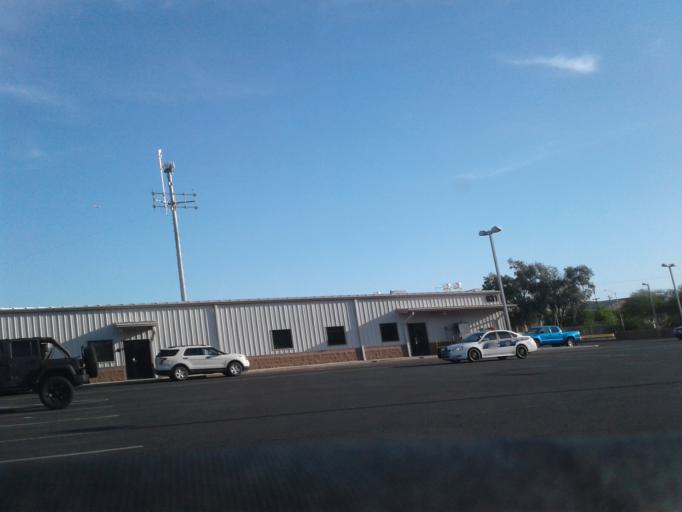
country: US
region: Arizona
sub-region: Maricopa County
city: Phoenix
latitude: 33.4423
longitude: -112.0643
